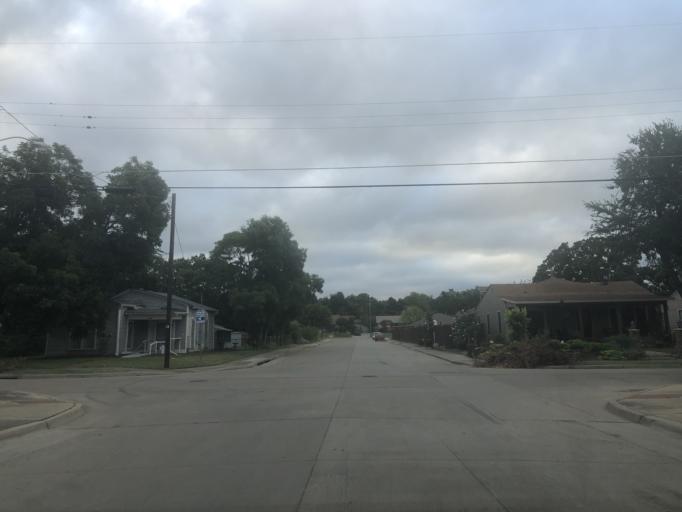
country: US
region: Texas
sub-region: Dallas County
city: University Park
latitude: 32.8309
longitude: -96.8554
